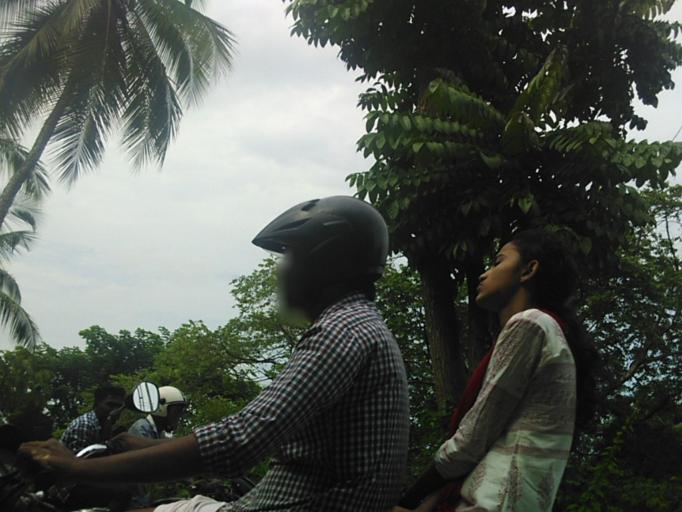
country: IN
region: Kerala
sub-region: Kozhikode
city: Kozhikode
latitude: 11.2827
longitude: 75.8032
